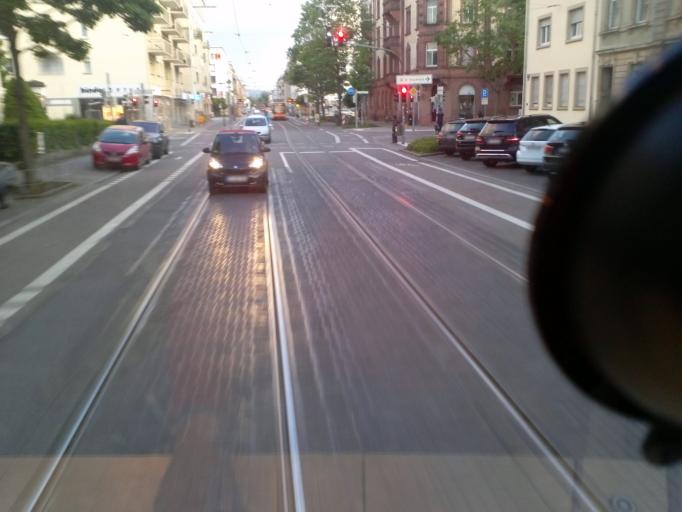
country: DE
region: Baden-Wuerttemberg
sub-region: Karlsruhe Region
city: Karlsruhe
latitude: 48.9987
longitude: 8.3938
